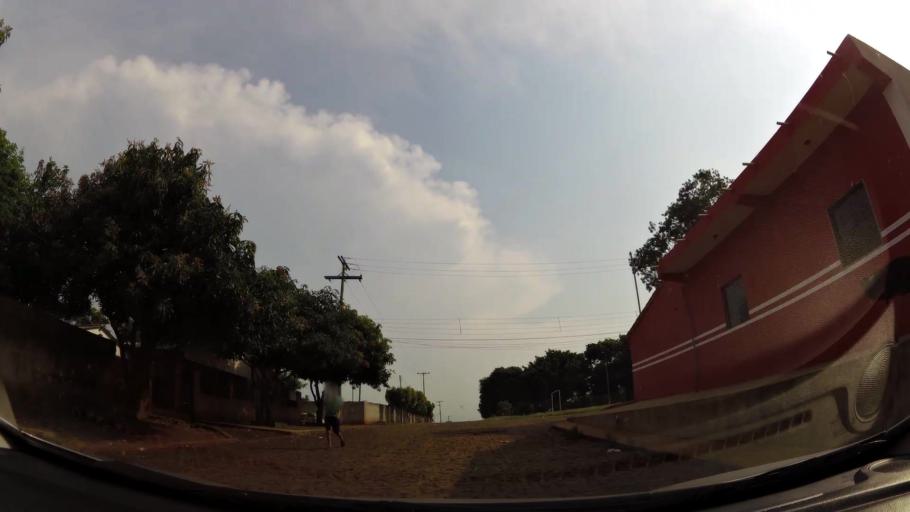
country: PY
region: Alto Parana
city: Ciudad del Este
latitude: -25.4900
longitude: -54.6445
